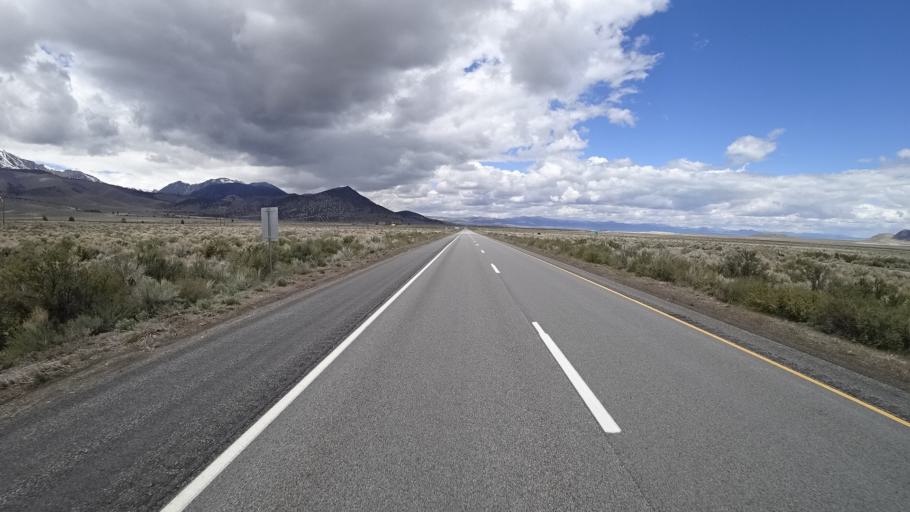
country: US
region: California
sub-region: Mono County
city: Mammoth Lakes
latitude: 37.8802
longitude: -119.0901
